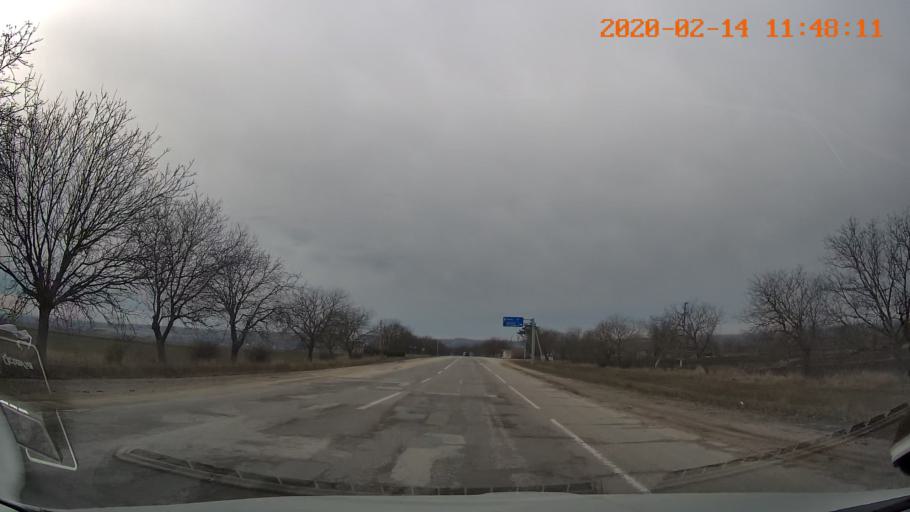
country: MD
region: Briceni
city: Briceni
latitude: 48.3102
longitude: 26.9549
